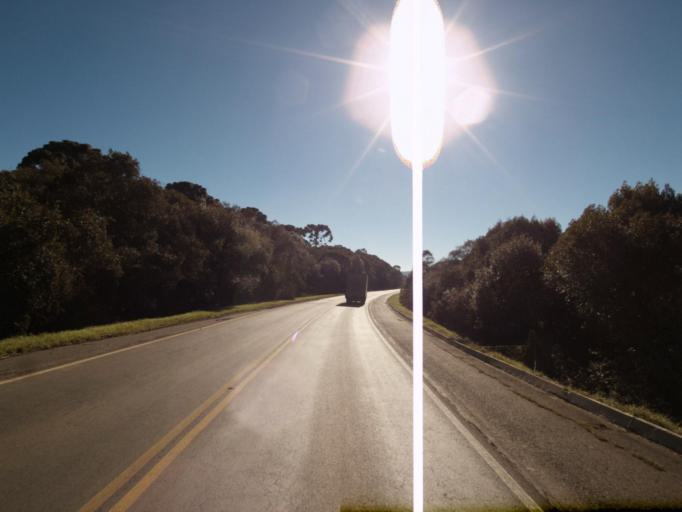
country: BR
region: Santa Catarina
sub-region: Concordia
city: Concordia
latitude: -26.9402
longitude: -51.8220
